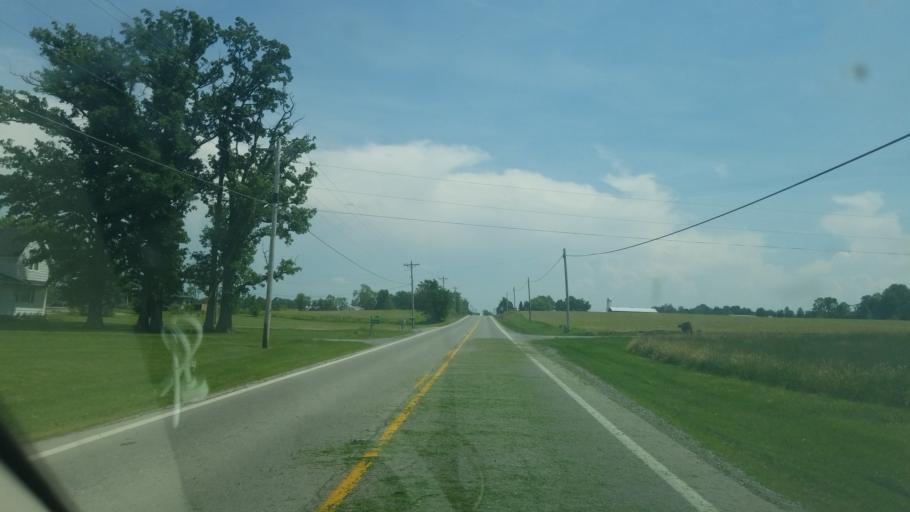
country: US
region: Ohio
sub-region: Logan County
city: Northwood
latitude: 40.4879
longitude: -83.7411
